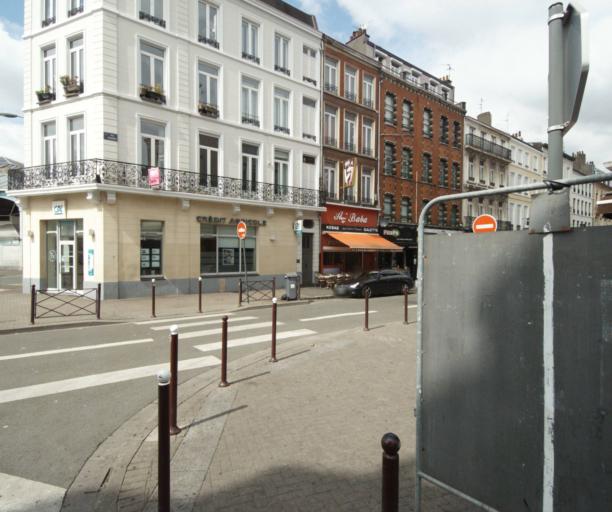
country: FR
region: Nord-Pas-de-Calais
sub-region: Departement du Nord
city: Lille
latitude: 50.6322
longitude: 3.0550
